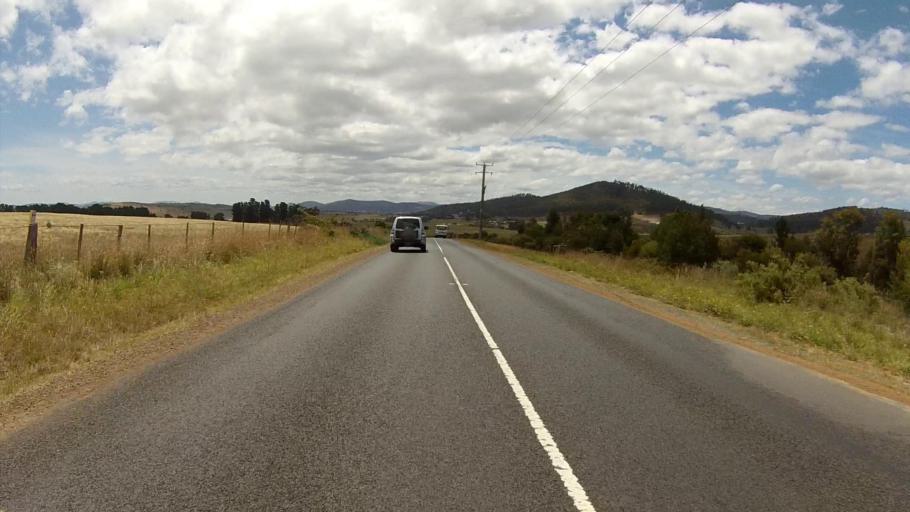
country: AU
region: Tasmania
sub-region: Sorell
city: Sorell
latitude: -42.8123
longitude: 147.6135
